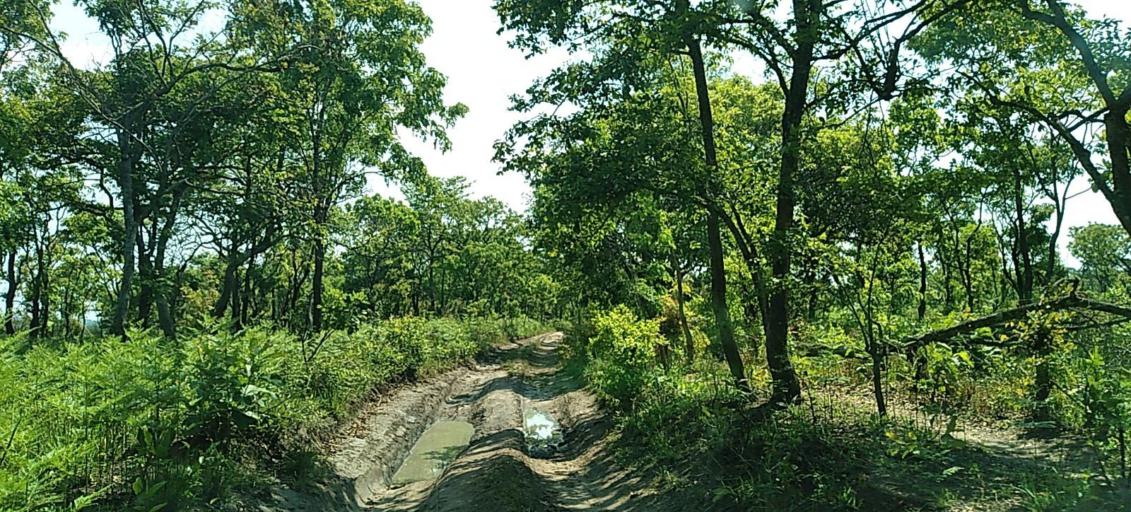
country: CD
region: Katanga
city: Kolwezi
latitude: -11.2603
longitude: 25.0095
